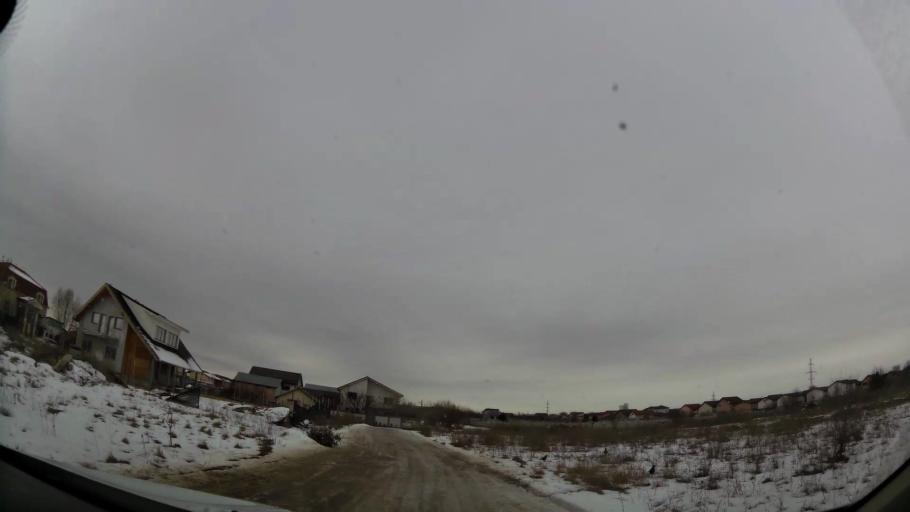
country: RO
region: Ilfov
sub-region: Comuna Pantelimon
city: Pantelimon
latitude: 44.4566
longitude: 26.2187
